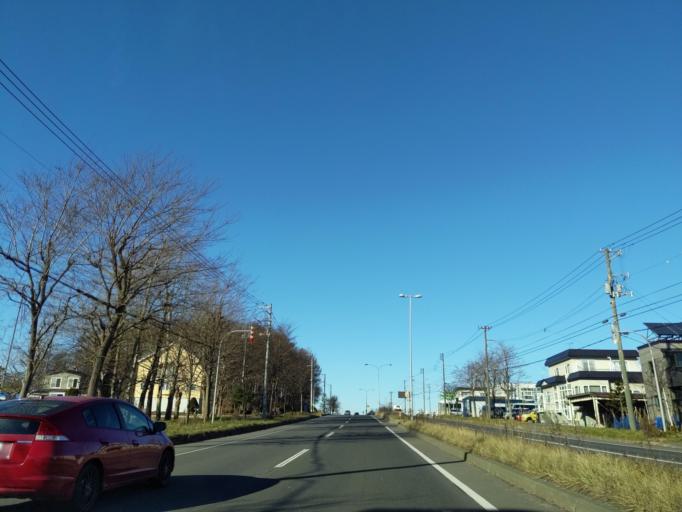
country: JP
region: Hokkaido
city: Kitahiroshima
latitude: 42.9450
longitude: 141.5016
